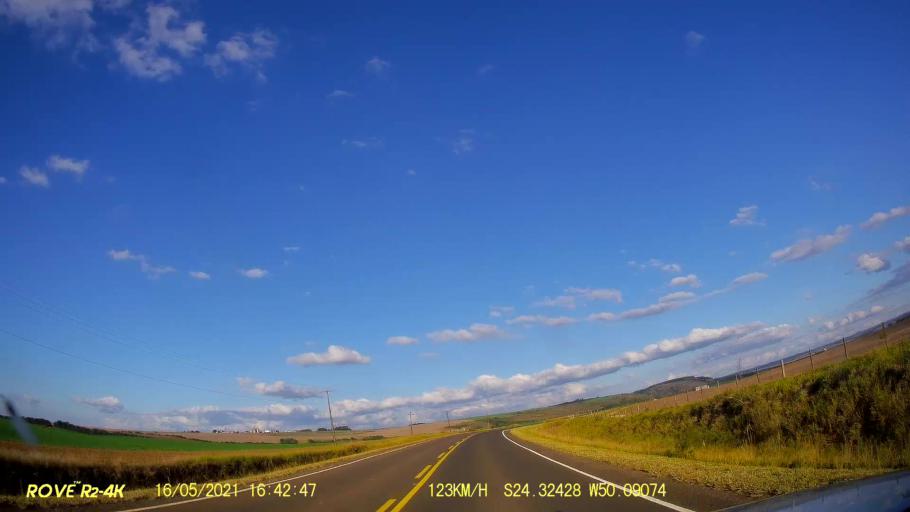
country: BR
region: Parana
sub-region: Pirai Do Sul
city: Pirai do Sul
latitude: -24.3250
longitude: -50.0909
